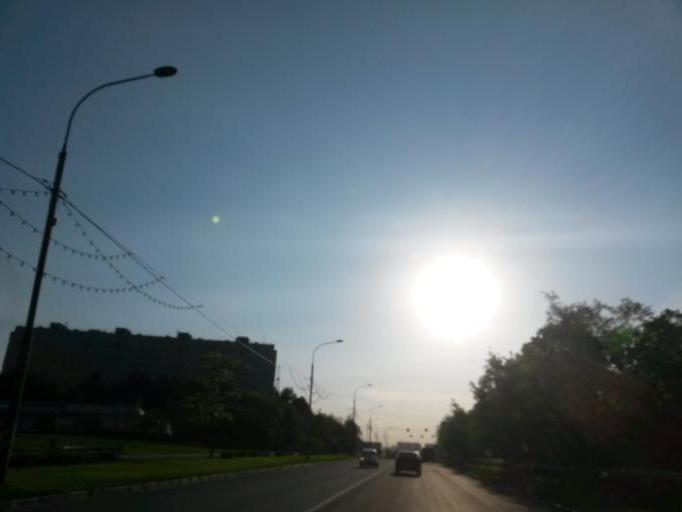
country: RU
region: Moskovskaya
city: Biryulevo Zapadnoye
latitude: 55.5875
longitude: 37.6433
